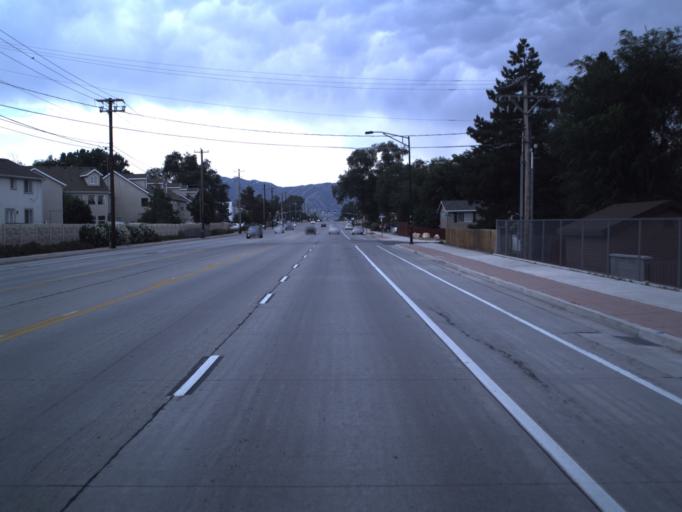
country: US
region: Utah
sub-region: Salt Lake County
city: White City
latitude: 40.5628
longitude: -111.8722
